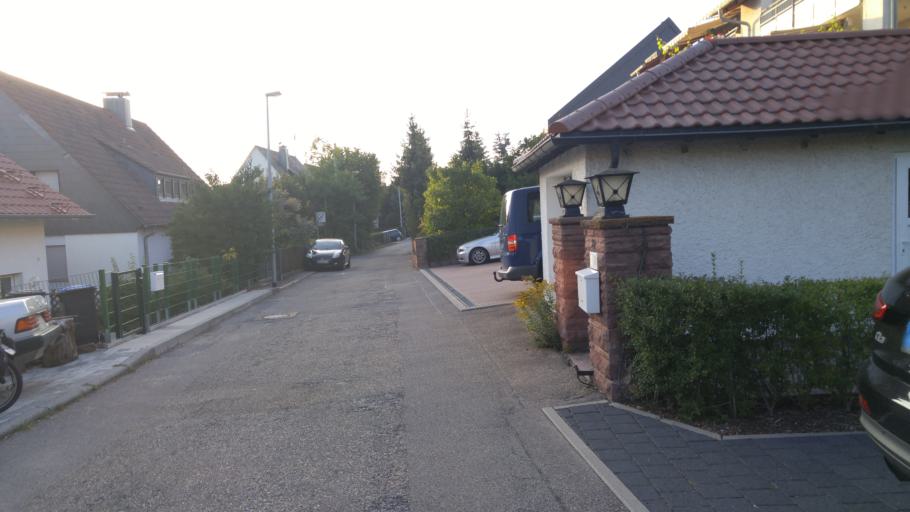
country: DE
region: Baden-Wuerttemberg
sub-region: Regierungsbezirk Stuttgart
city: Leonberg
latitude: 48.8051
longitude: 9.0126
